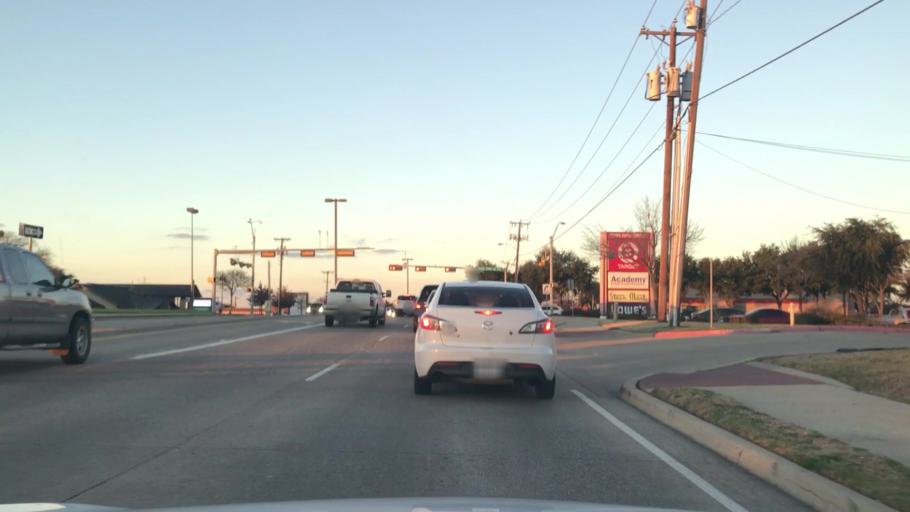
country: US
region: Texas
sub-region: Rockwall County
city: Rockwall
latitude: 32.8932
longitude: -96.4710
